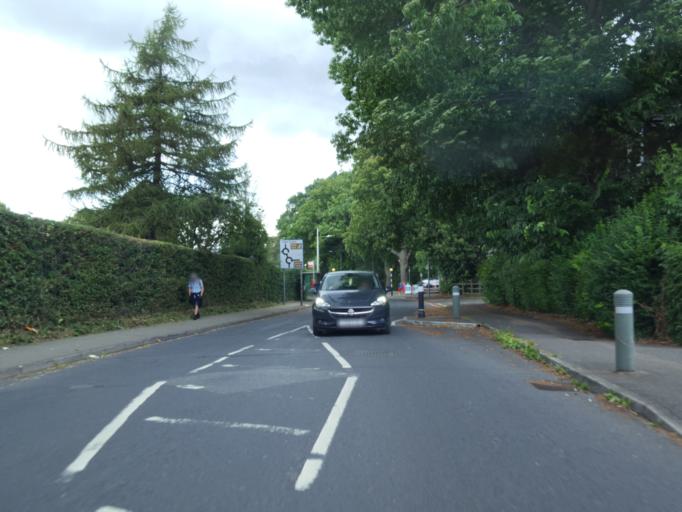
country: GB
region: England
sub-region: Kent
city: Maidstone
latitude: 51.2650
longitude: 0.5347
